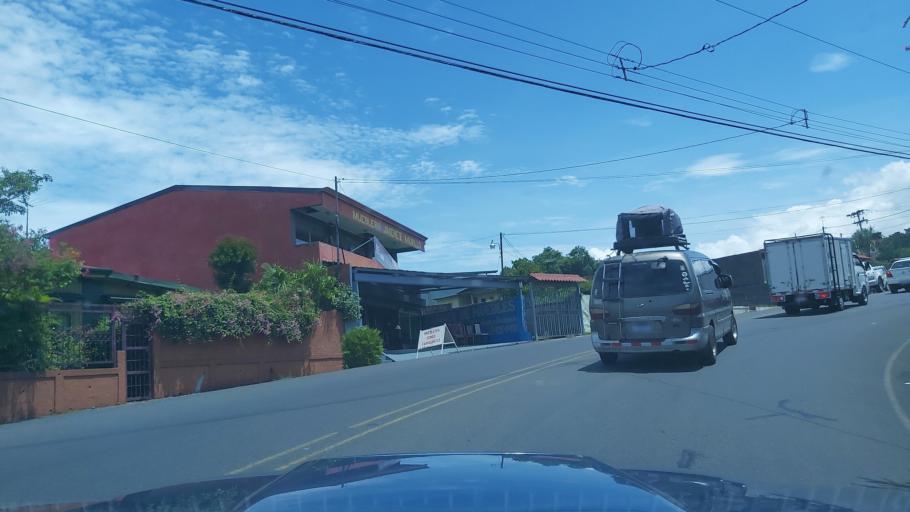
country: CR
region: Alajuela
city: San Juan
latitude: 10.0881
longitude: -84.3453
